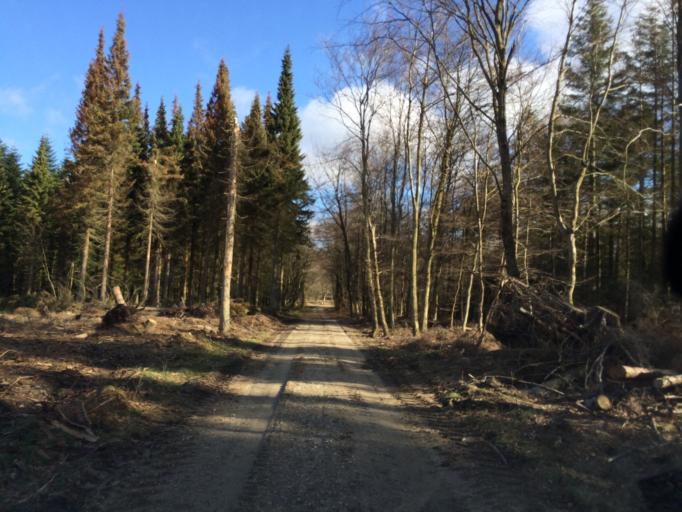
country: DK
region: Central Jutland
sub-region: Holstebro Kommune
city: Ulfborg
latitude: 56.2524
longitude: 8.4594
